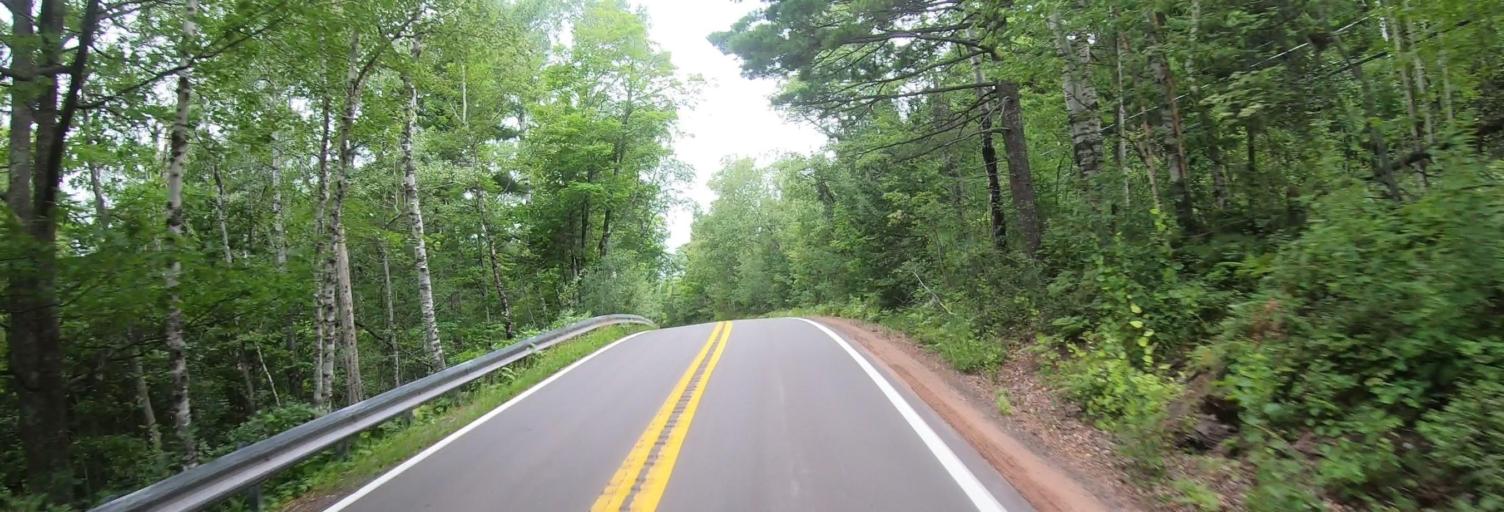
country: US
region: Michigan
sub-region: Keweenaw County
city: Eagle River
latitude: 47.4615
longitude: -88.0872
